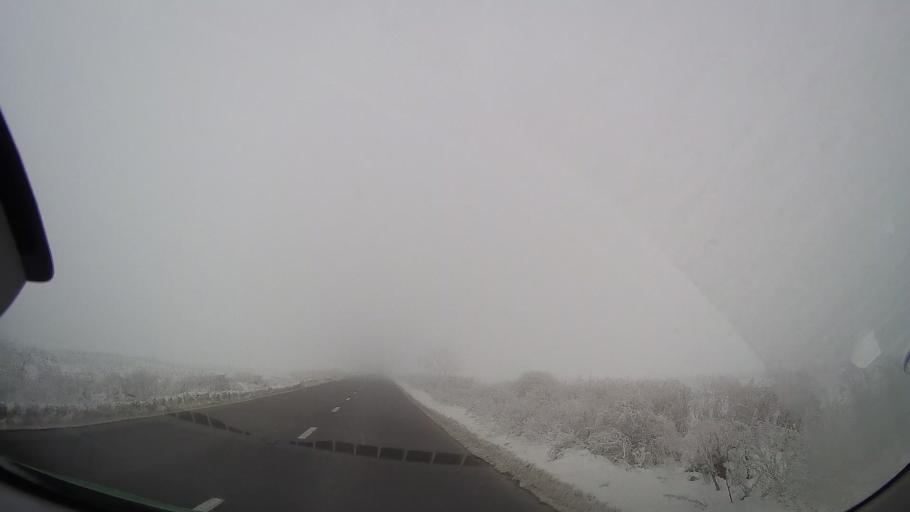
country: RO
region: Iasi
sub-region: Comuna Mircesti
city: Iugani
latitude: 47.0406
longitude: 26.8517
